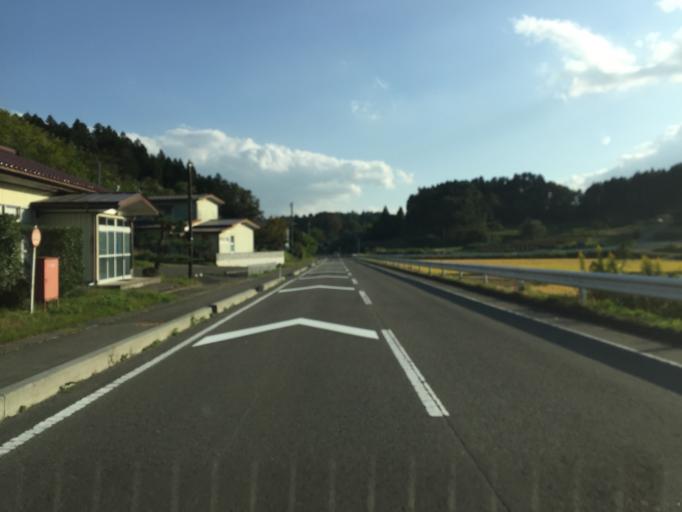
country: JP
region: Fukushima
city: Fukushima-shi
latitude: 37.6669
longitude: 140.5398
